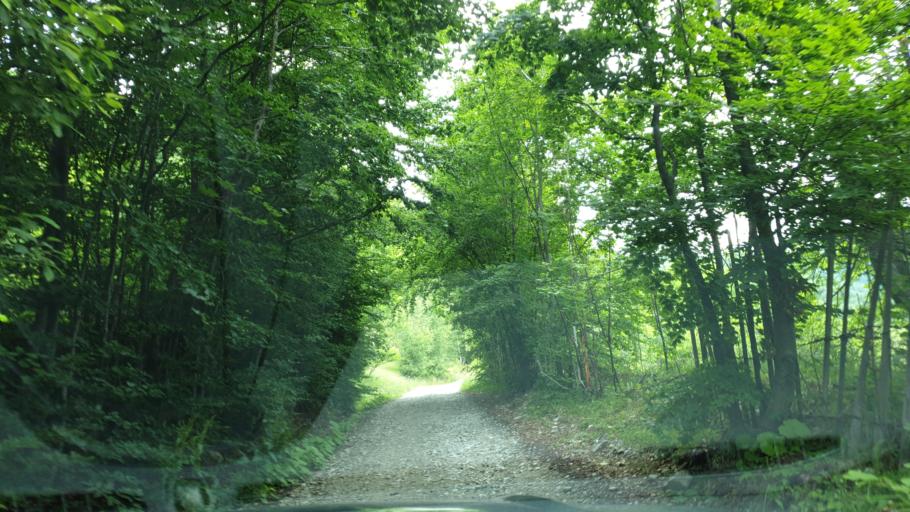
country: RO
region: Hunedoara
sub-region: Comuna Uricani
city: Uricani
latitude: 45.3069
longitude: 22.9822
